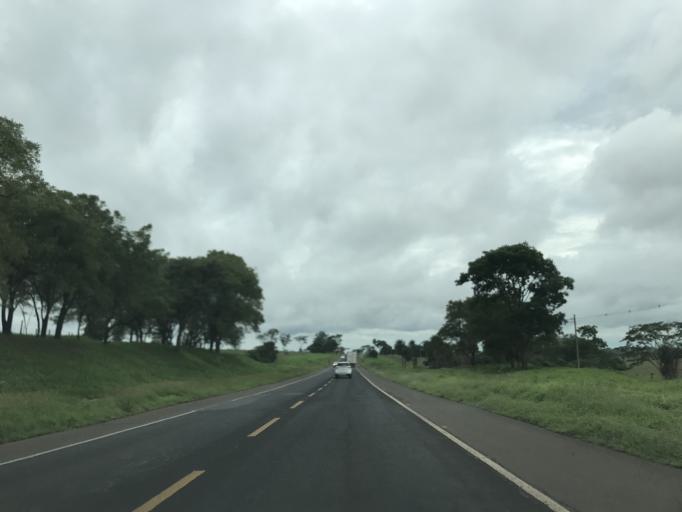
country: BR
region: Sao Paulo
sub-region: Nova Granada
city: Nova Granada
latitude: -20.4972
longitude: -49.3163
